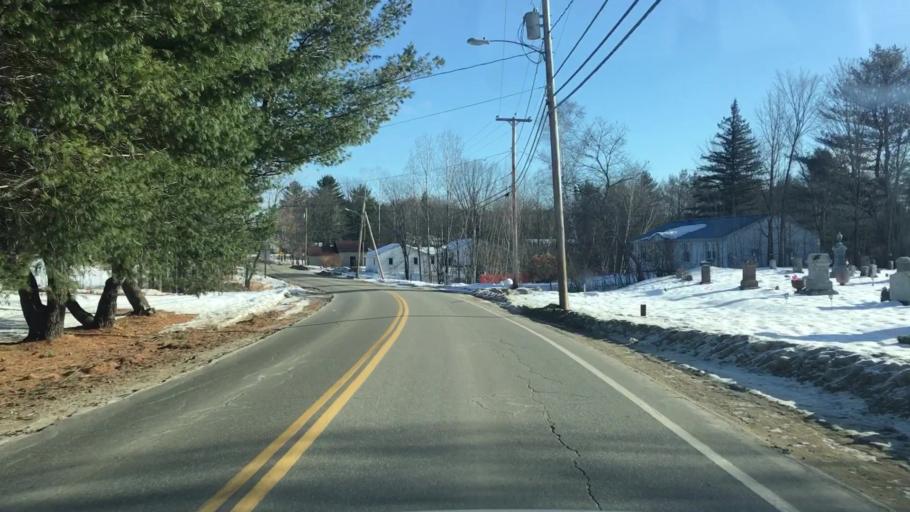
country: US
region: Maine
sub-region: Oxford County
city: West Paris
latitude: 44.3266
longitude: -70.5661
